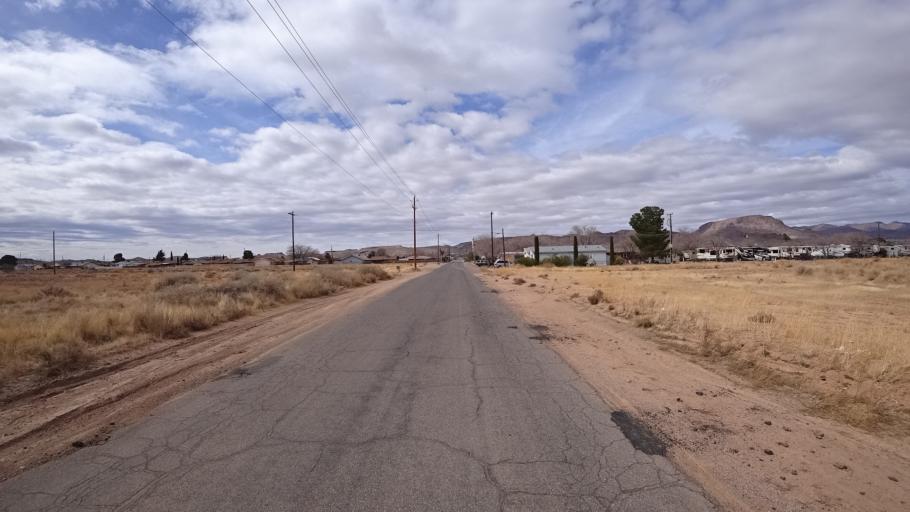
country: US
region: Arizona
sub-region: Mohave County
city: New Kingman-Butler
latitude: 35.2322
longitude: -114.0161
